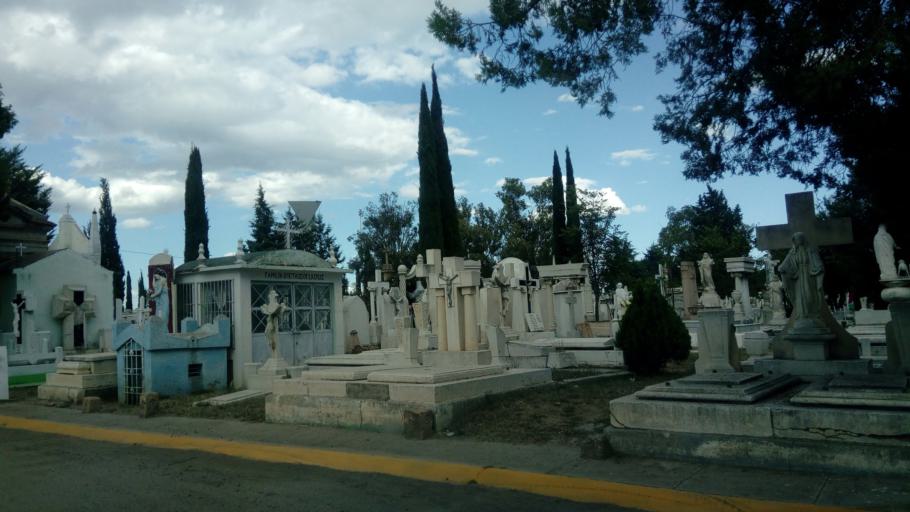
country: MX
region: Durango
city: Victoria de Durango
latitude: 24.0281
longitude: -104.6390
